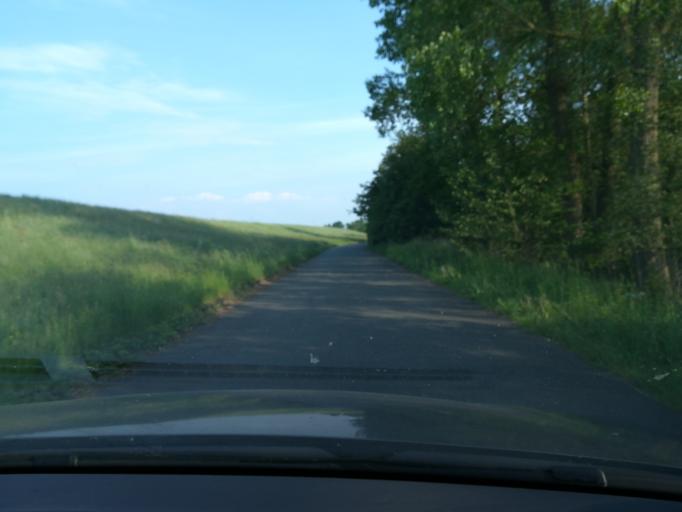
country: DE
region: Lower Saxony
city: Artlenburg
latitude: 53.3819
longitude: 10.4693
